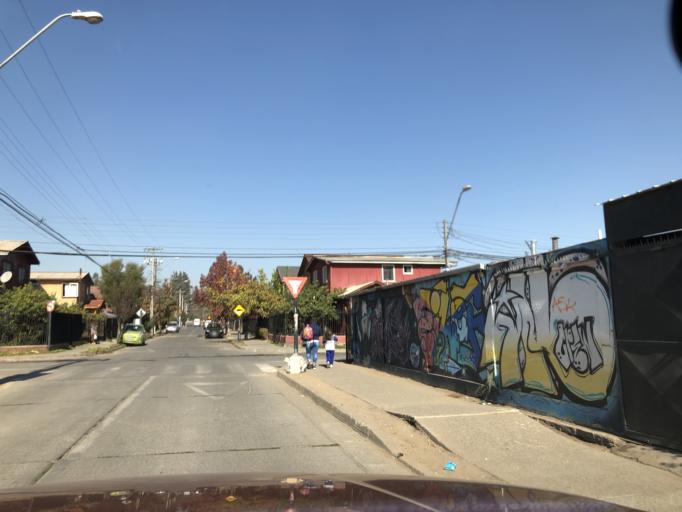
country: CL
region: Santiago Metropolitan
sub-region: Provincia de Cordillera
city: Puente Alto
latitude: -33.5664
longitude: -70.5821
